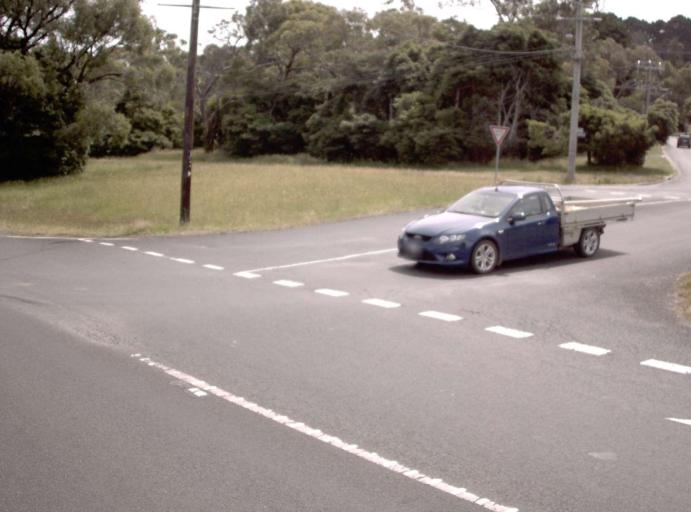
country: AU
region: Victoria
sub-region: Mornington Peninsula
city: Baxter
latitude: -38.1942
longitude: 145.1354
